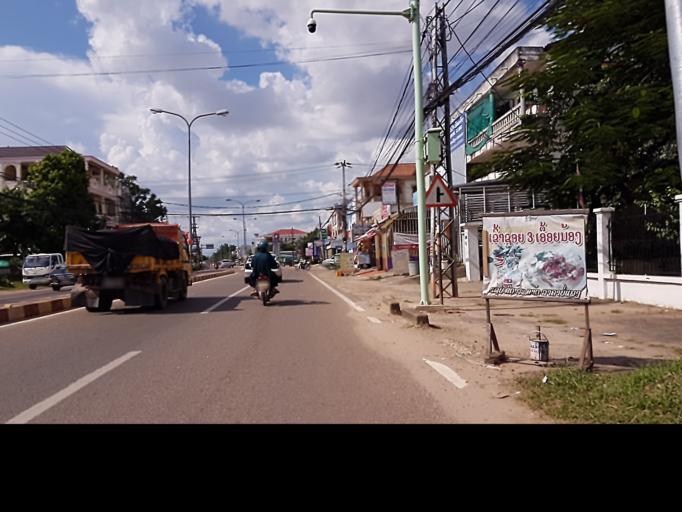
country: TH
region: Nong Khai
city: Si Chiang Mai
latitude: 17.9181
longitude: 102.6195
